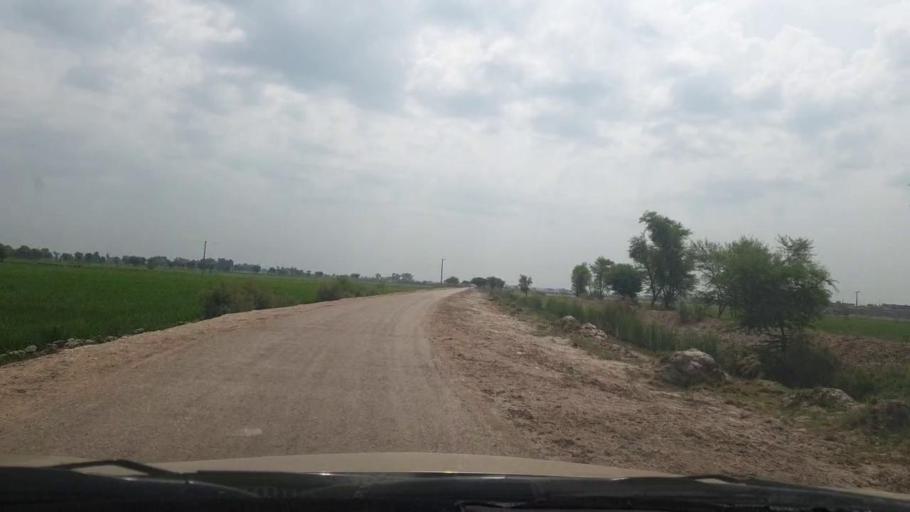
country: PK
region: Sindh
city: Miro Khan
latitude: 27.6975
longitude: 68.2016
